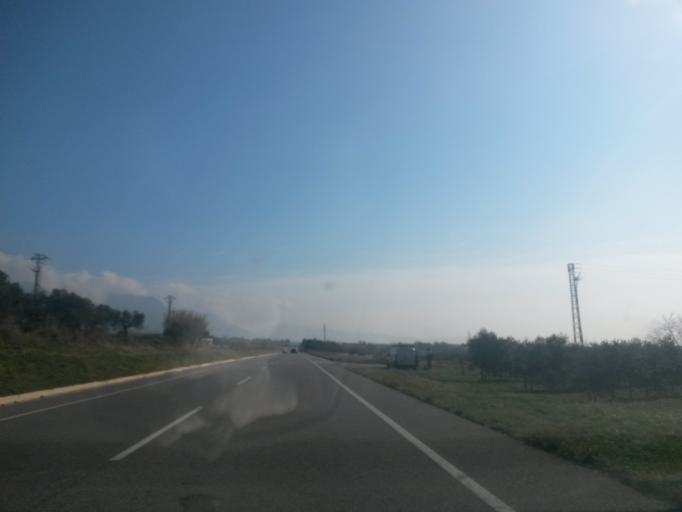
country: ES
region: Catalonia
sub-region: Provincia de Girona
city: Vilajuiga
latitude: 42.3215
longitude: 3.0968
